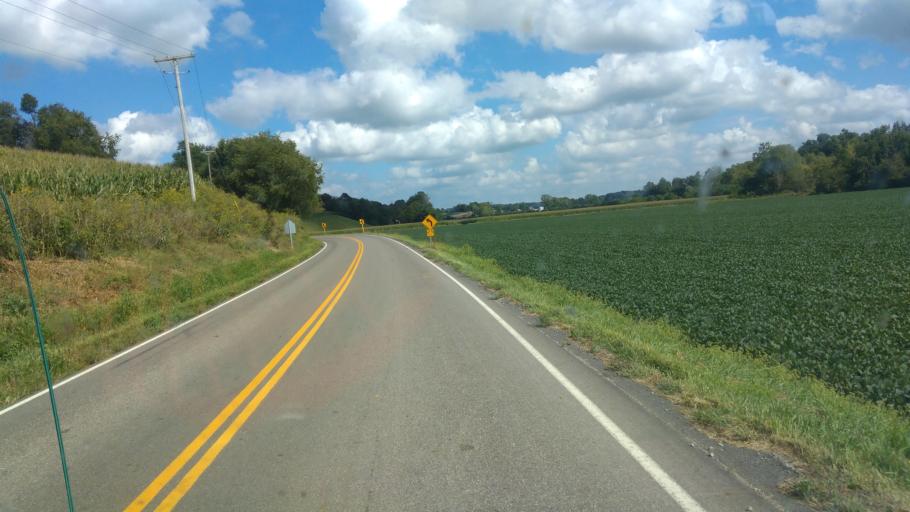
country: US
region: Ohio
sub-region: Holmes County
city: Millersburg
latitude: 40.6249
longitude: -81.8949
